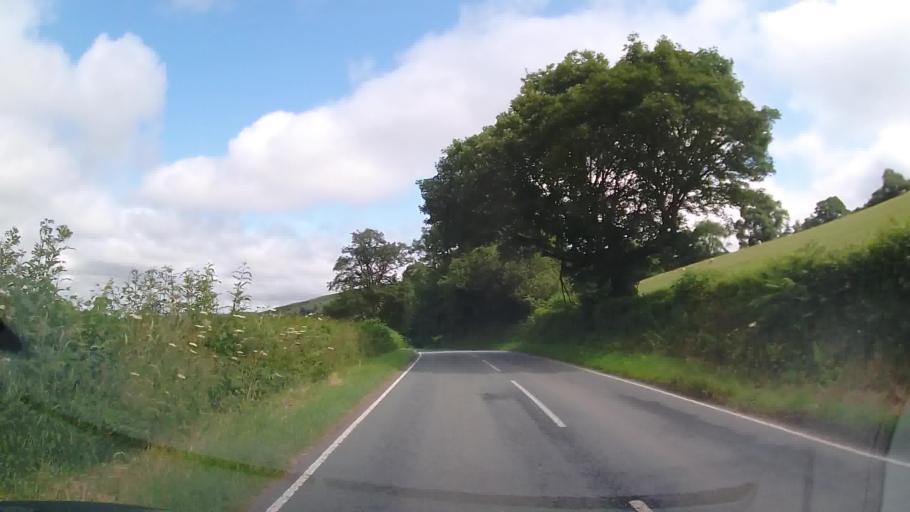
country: GB
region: Wales
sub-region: Sir Powys
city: Llangynog
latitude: 52.8150
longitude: -3.3680
